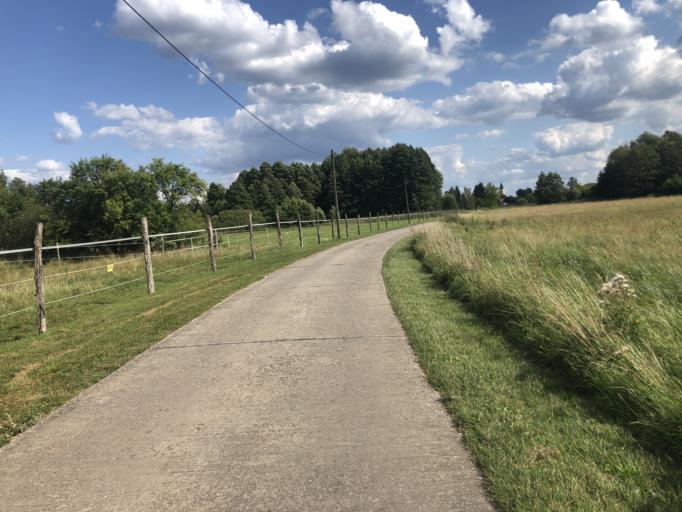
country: DE
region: Brandenburg
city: Mullrose
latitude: 52.2520
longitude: 14.4060
